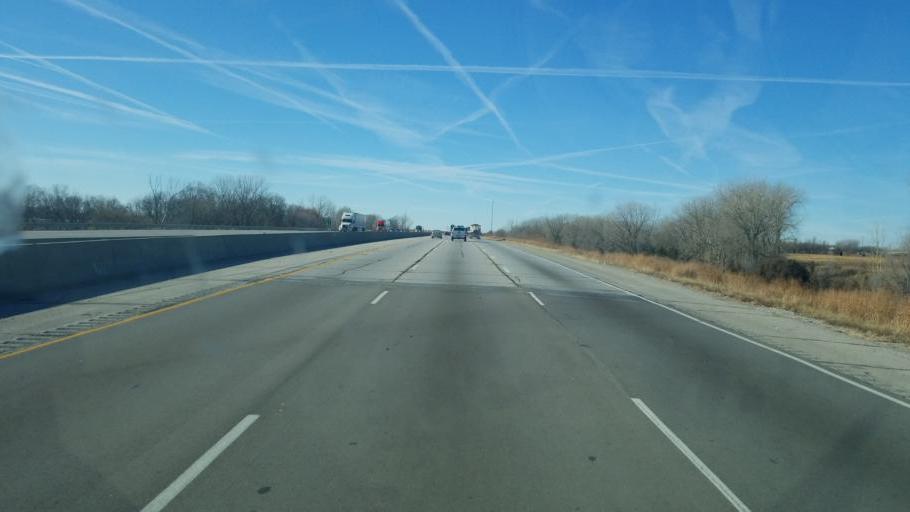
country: US
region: Iowa
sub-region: Polk County
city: Des Moines
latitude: 41.6543
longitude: -93.5614
